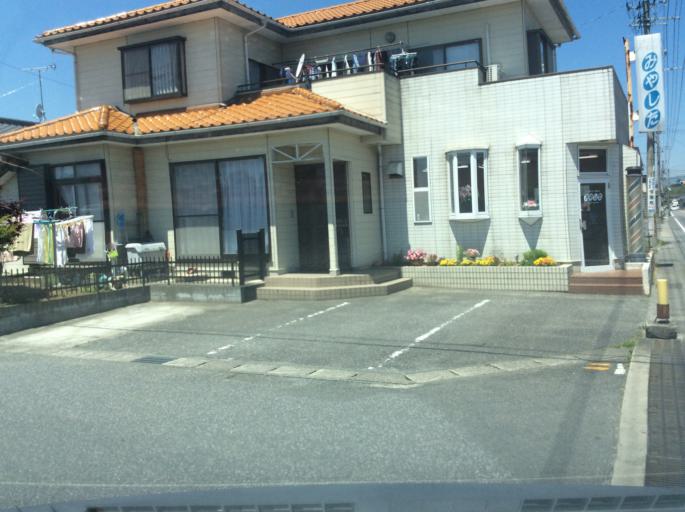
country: JP
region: Fukushima
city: Iwaki
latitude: 37.0849
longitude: 140.8776
